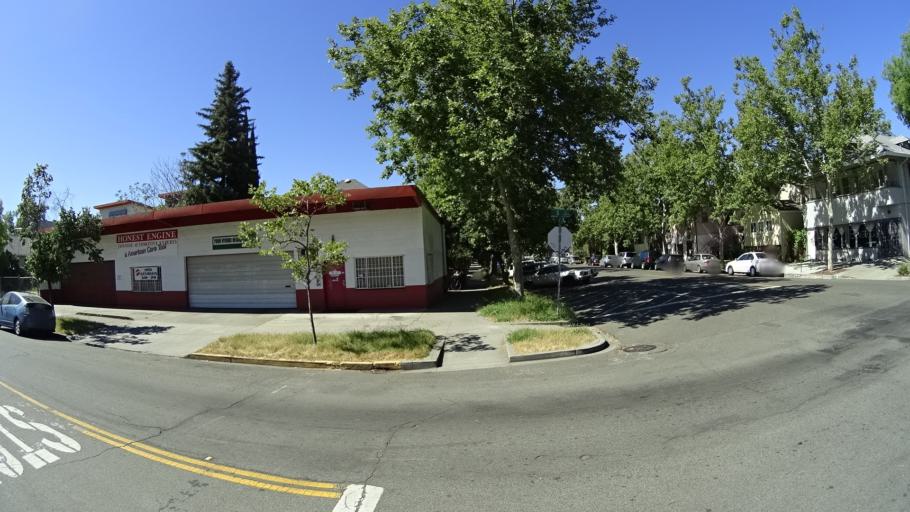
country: US
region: California
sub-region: Sacramento County
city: Sacramento
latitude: 38.5639
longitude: -121.4734
